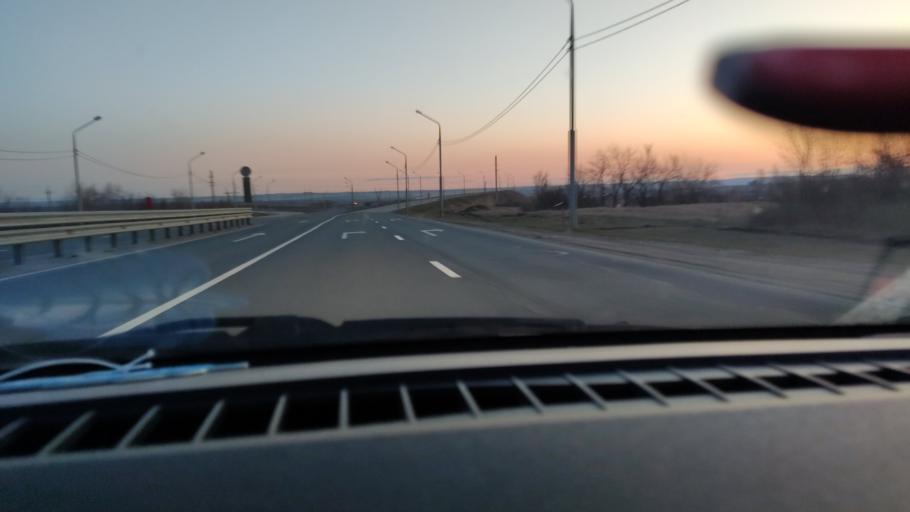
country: RU
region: Saratov
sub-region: Saratovskiy Rayon
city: Saratov
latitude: 51.6638
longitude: 45.9996
